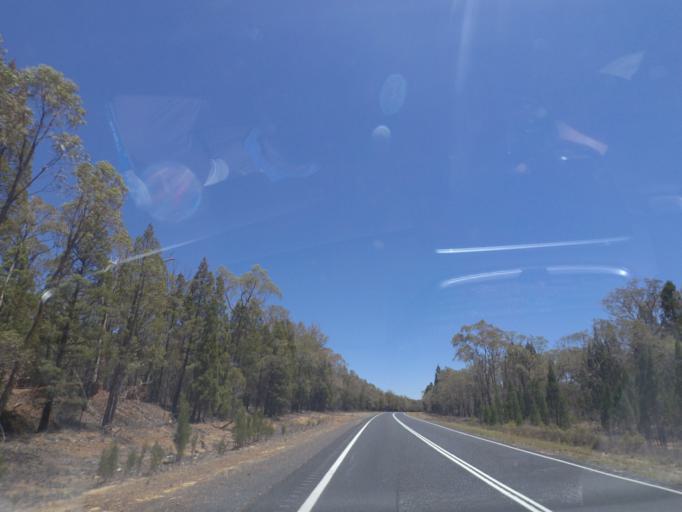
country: AU
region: New South Wales
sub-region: Warrumbungle Shire
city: Coonabarabran
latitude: -31.1976
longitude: 149.3487
